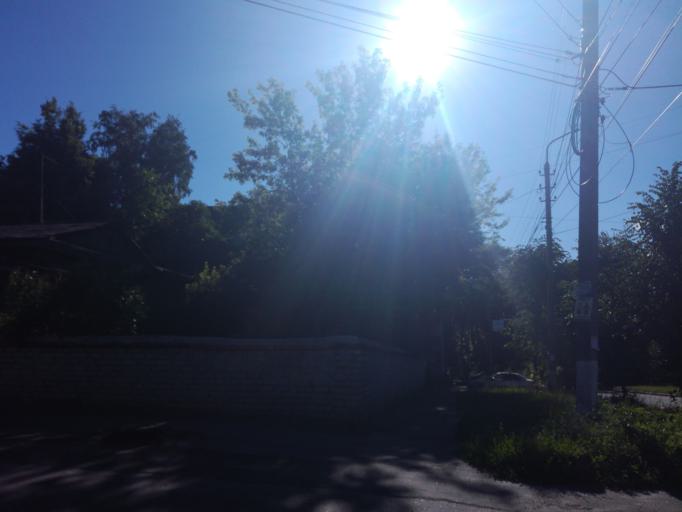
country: RU
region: Kursk
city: Kursk
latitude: 51.7464
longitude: 36.1831
